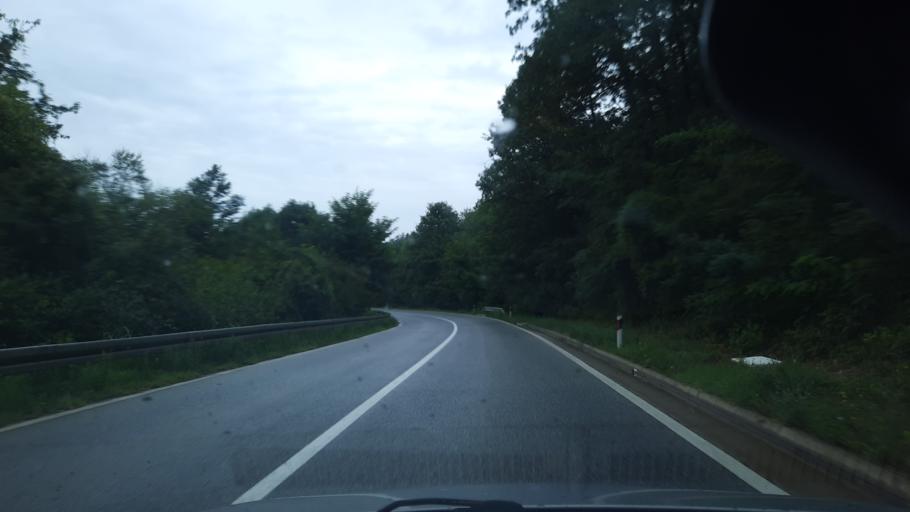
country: RS
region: Central Serbia
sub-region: Sumadijski Okrug
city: Knic
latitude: 43.8454
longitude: 20.7706
